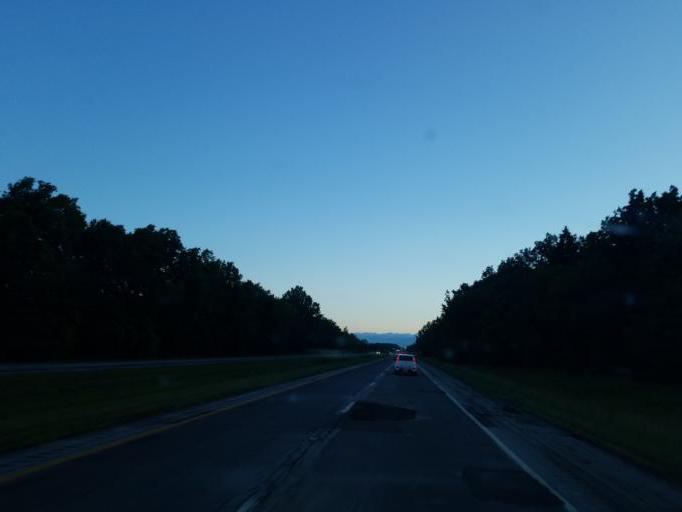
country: US
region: Ohio
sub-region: Summit County
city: Clinton
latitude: 40.9548
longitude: -81.6582
